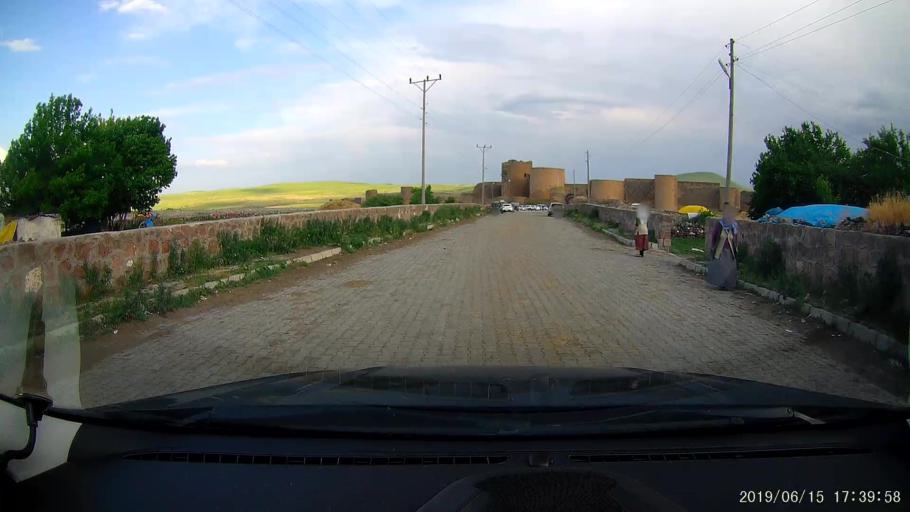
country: TR
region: Kars
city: Basgedikler
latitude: 40.5135
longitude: 43.5719
